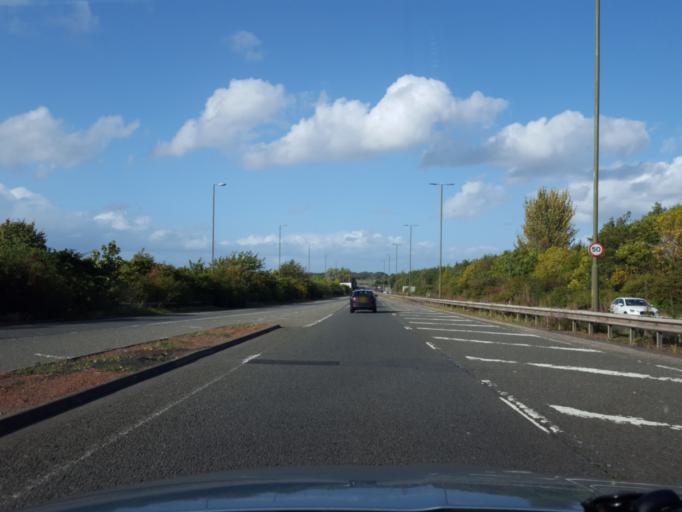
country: GB
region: Scotland
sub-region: Edinburgh
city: Currie
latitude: 55.9323
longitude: -3.3199
